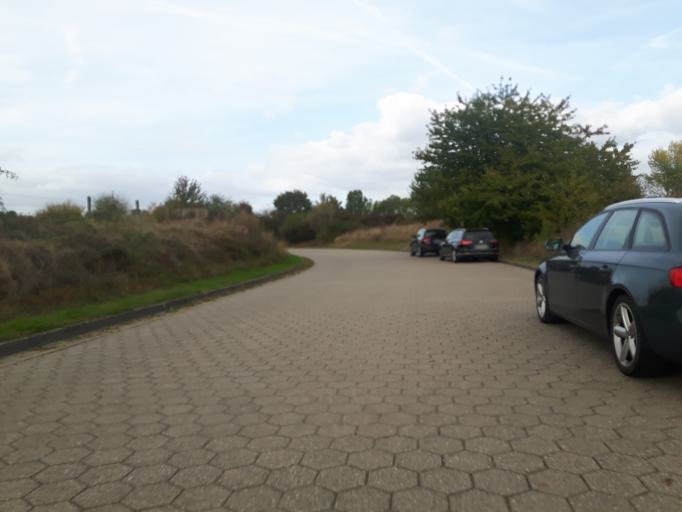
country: DE
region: Rheinland-Pfalz
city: Urmitz
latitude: 50.4183
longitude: 7.4973
